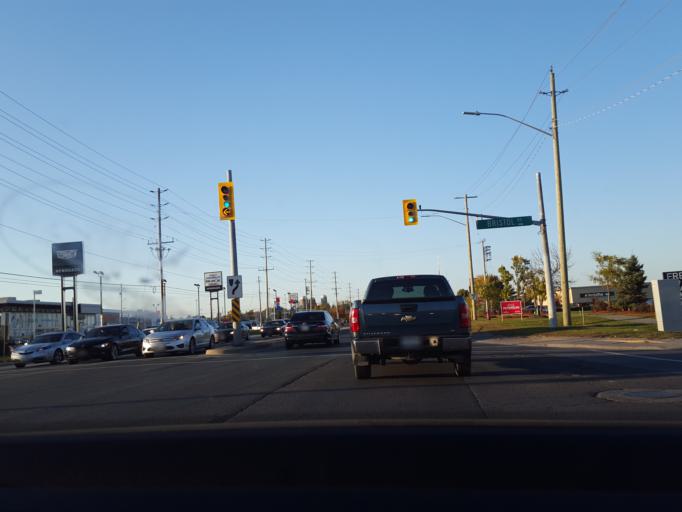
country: CA
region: Ontario
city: Newmarket
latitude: 44.0679
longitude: -79.4834
